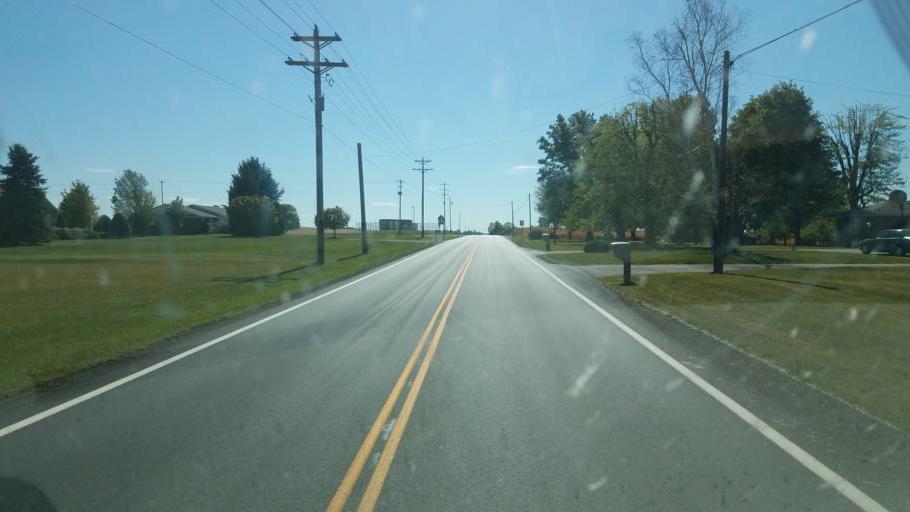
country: US
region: Ohio
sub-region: Huron County
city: Willard
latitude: 40.9507
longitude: -82.8538
